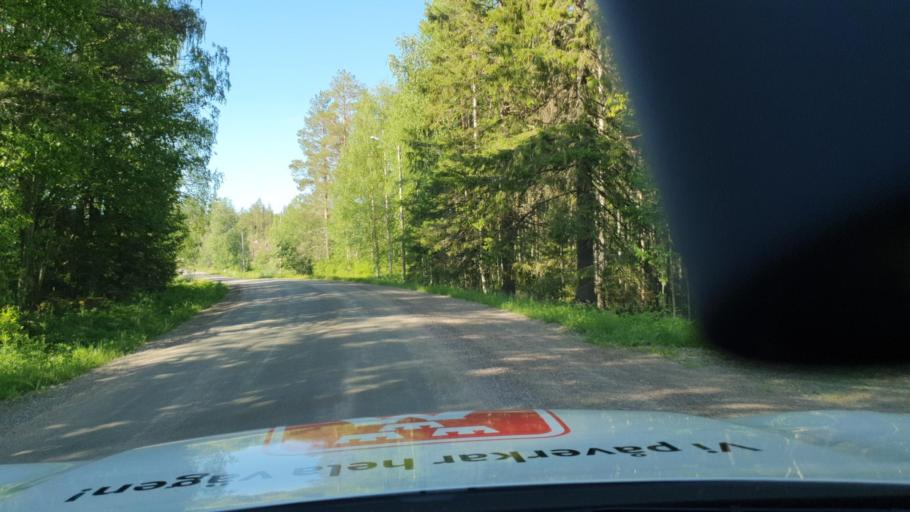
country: SE
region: Vaesterbotten
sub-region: Vannas Kommun
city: Vaennaes
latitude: 63.8348
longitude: 19.6322
